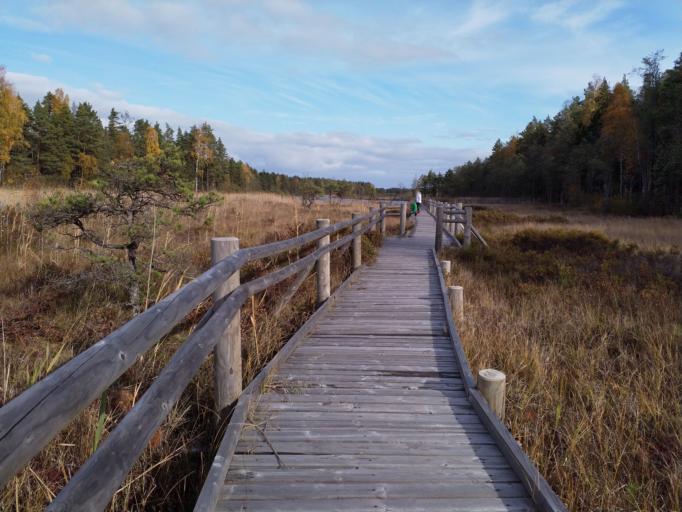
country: LV
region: Dundaga
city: Dundaga
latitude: 57.6511
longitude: 22.2566
